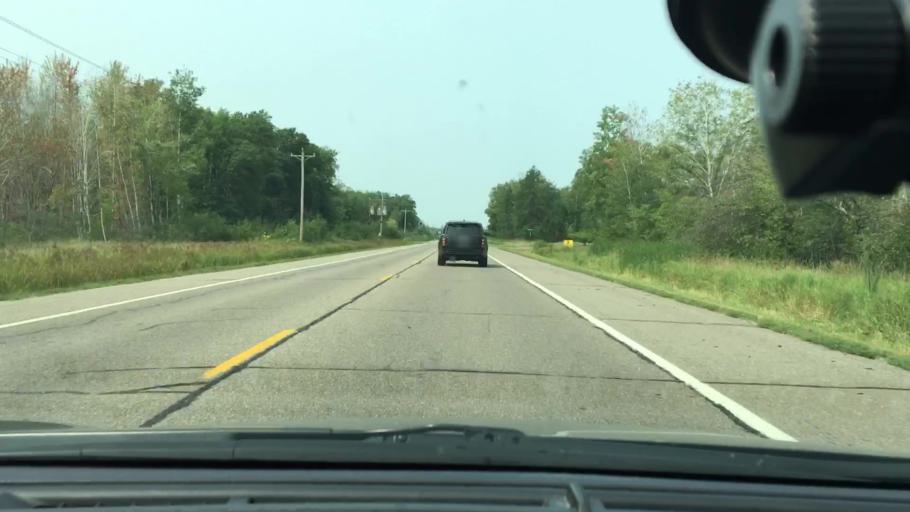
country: US
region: Minnesota
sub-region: Crow Wing County
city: Brainerd
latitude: 46.3984
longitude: -94.2100
